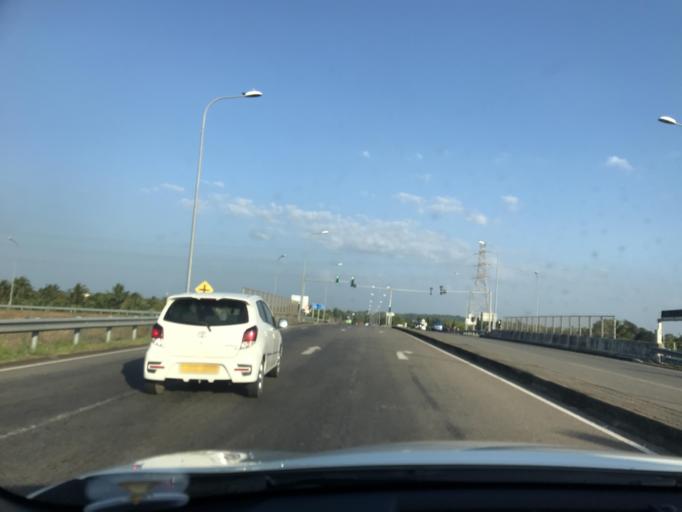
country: LK
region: Western
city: Ja Ela
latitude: 7.0816
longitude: 79.8770
